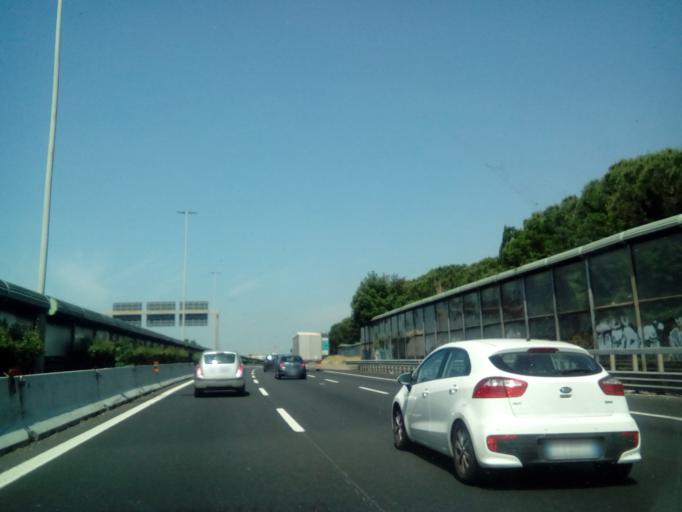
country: IT
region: Latium
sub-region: Citta metropolitana di Roma Capitale
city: Vitinia
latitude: 41.8032
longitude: 12.4352
